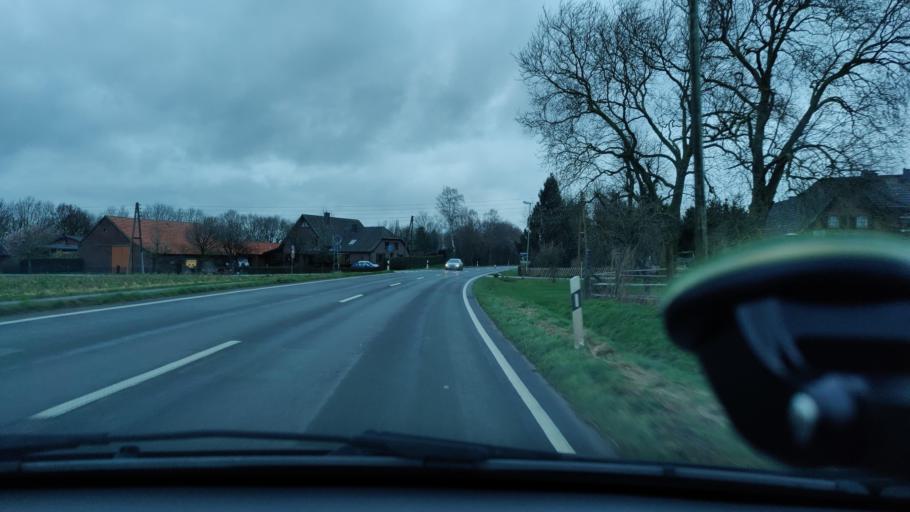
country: DE
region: North Rhine-Westphalia
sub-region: Regierungsbezirk Dusseldorf
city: Weeze
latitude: 51.5776
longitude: 6.1816
